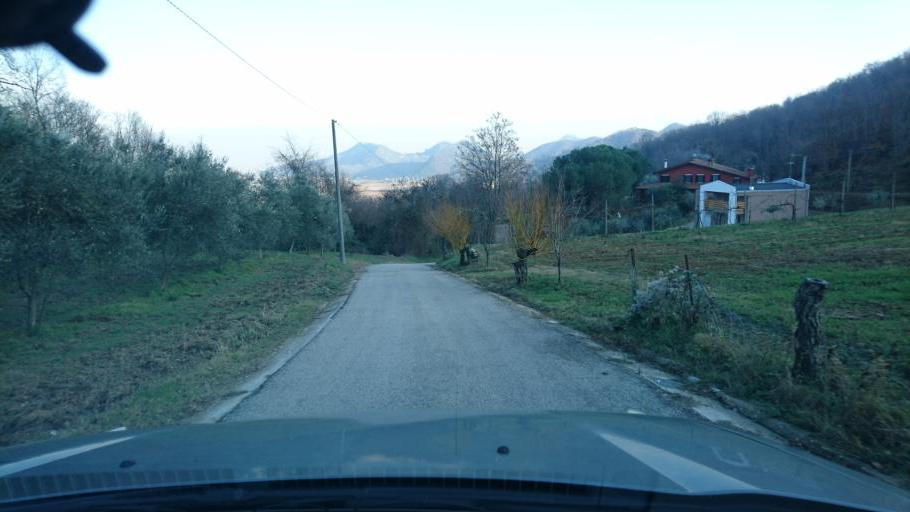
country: IT
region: Veneto
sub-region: Provincia di Padova
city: Torreglia
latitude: 45.3275
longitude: 11.7197
